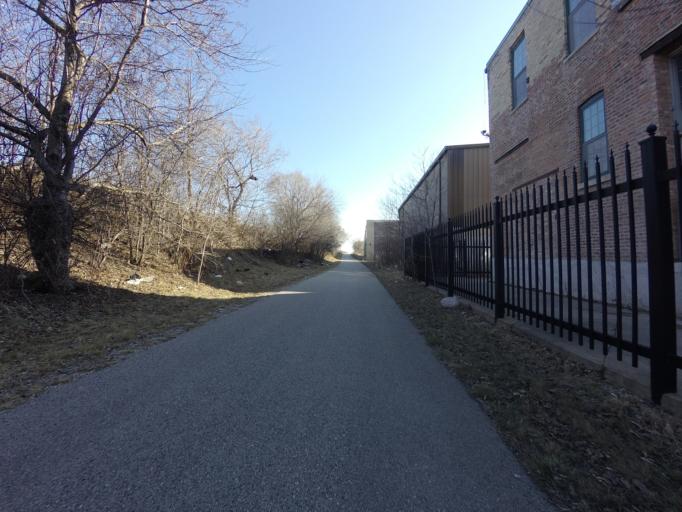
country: US
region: Wisconsin
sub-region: Milwaukee County
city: Milwaukee
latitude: 43.0197
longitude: -87.9090
